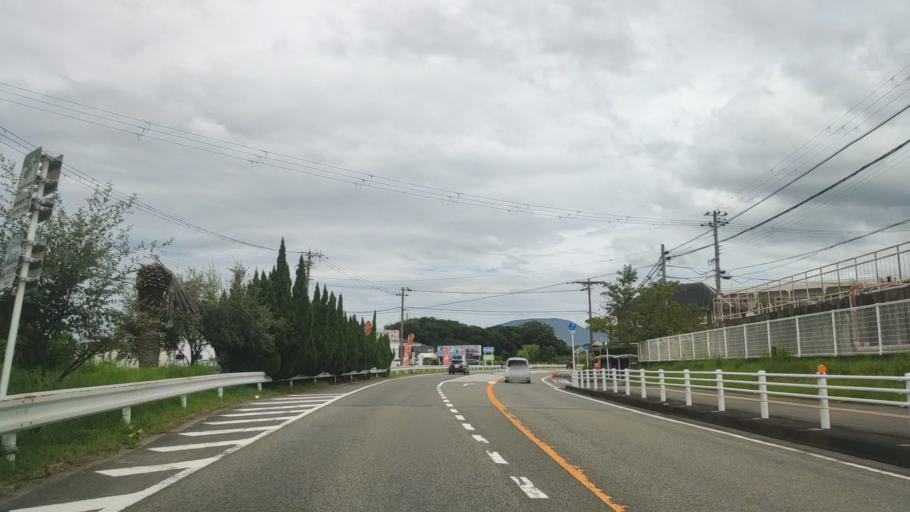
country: JP
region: Wakayama
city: Tanabe
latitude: 33.6995
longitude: 135.3887
